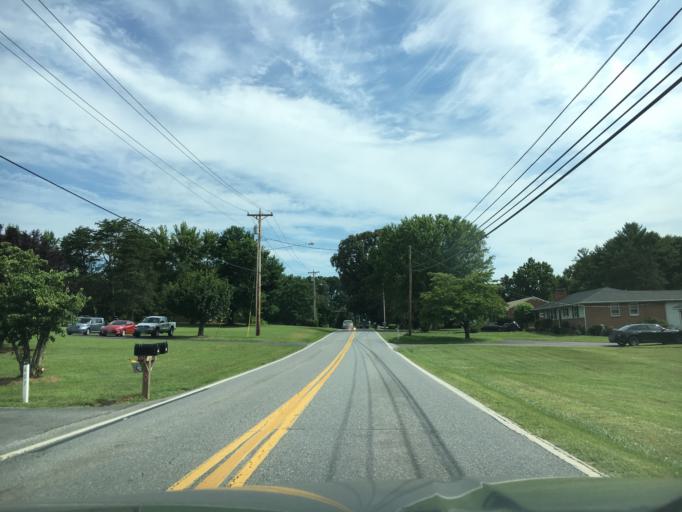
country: US
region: Virginia
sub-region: Campbell County
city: Timberlake
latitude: 37.3620
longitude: -79.2291
